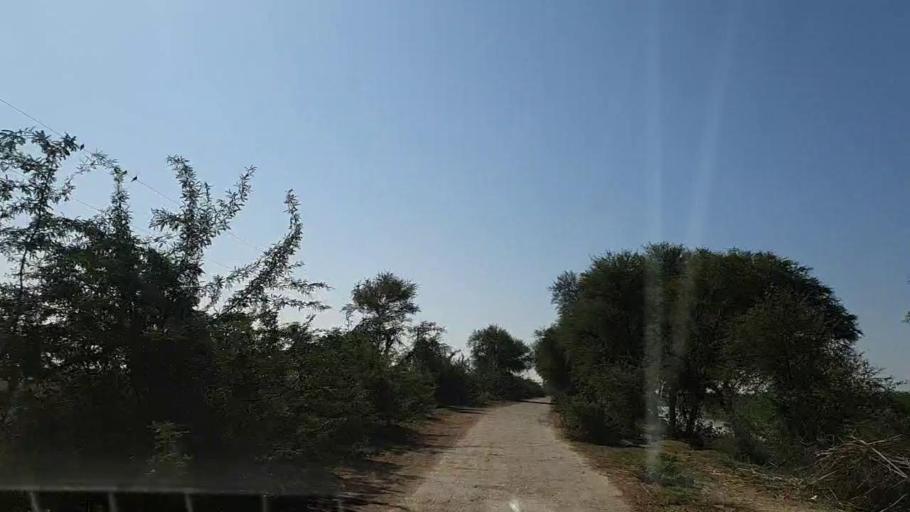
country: PK
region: Sindh
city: Chuhar Jamali
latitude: 24.5819
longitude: 68.0473
